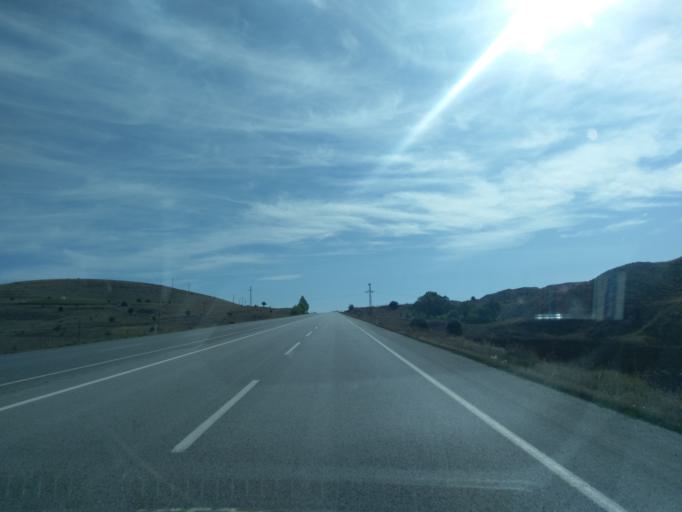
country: TR
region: Sivas
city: Imranli
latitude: 39.8841
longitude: 38.0393
